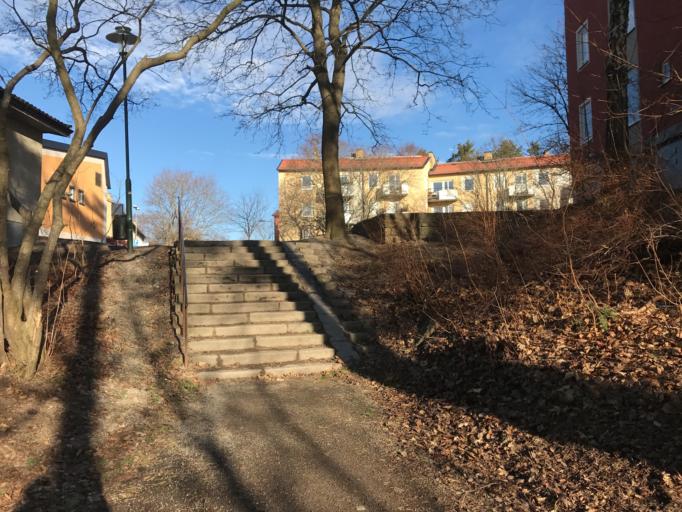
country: SE
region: Stockholm
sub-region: Nacka Kommun
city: Nacka
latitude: 59.2785
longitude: 18.1255
